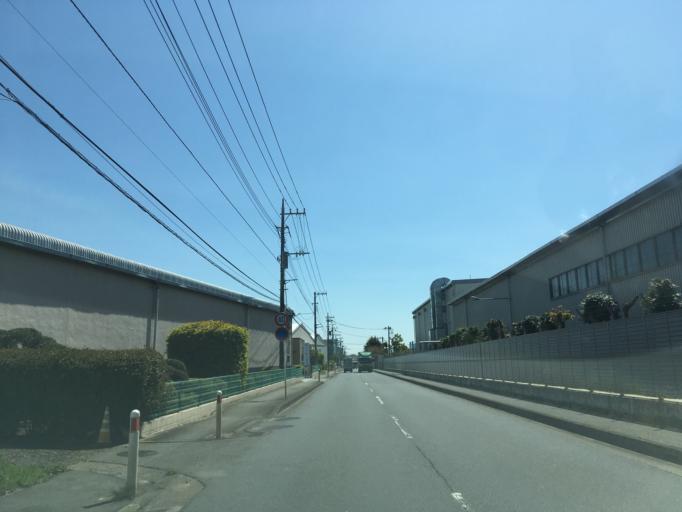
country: JP
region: Tokyo
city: Hachioji
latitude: 35.5666
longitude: 139.3374
